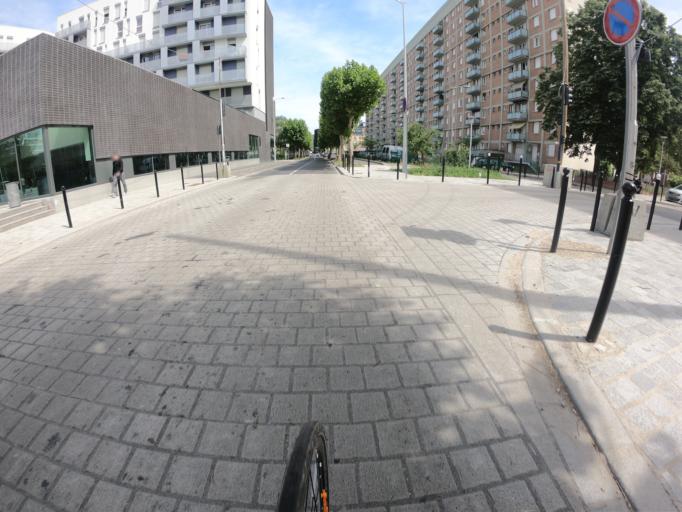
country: FR
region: Ile-de-France
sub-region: Departement du Val-de-Marne
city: Gentilly
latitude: 48.8145
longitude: 2.3329
